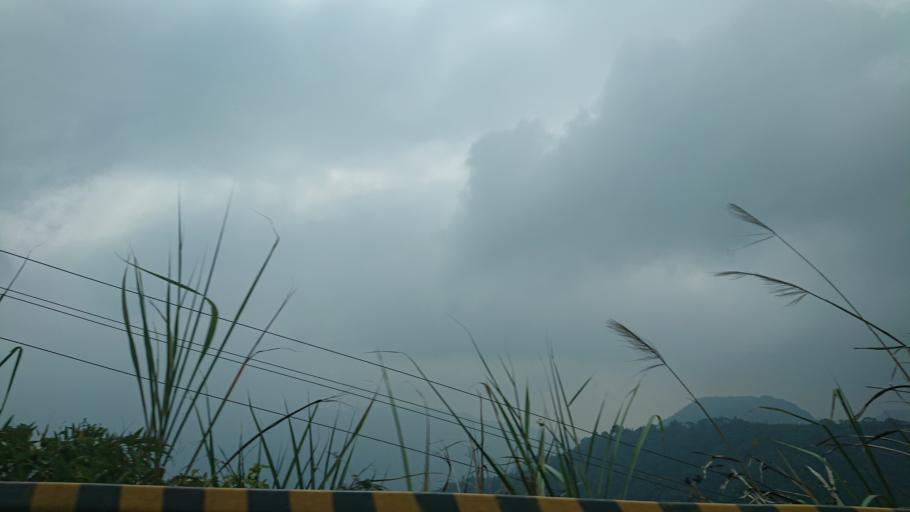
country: TW
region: Taiwan
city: Lugu
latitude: 23.6021
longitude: 120.7018
